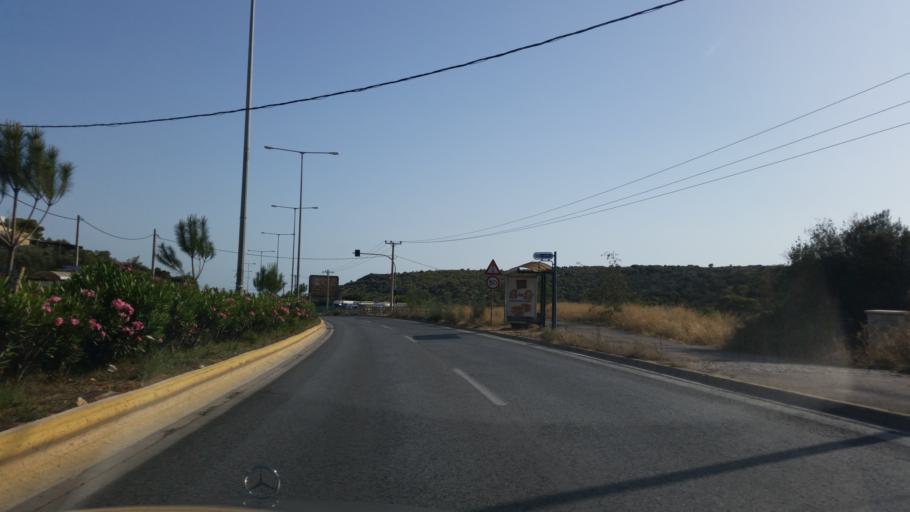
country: GR
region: Attica
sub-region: Nomarchia Anatolikis Attikis
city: Kitsi
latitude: 37.8555
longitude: 23.8318
